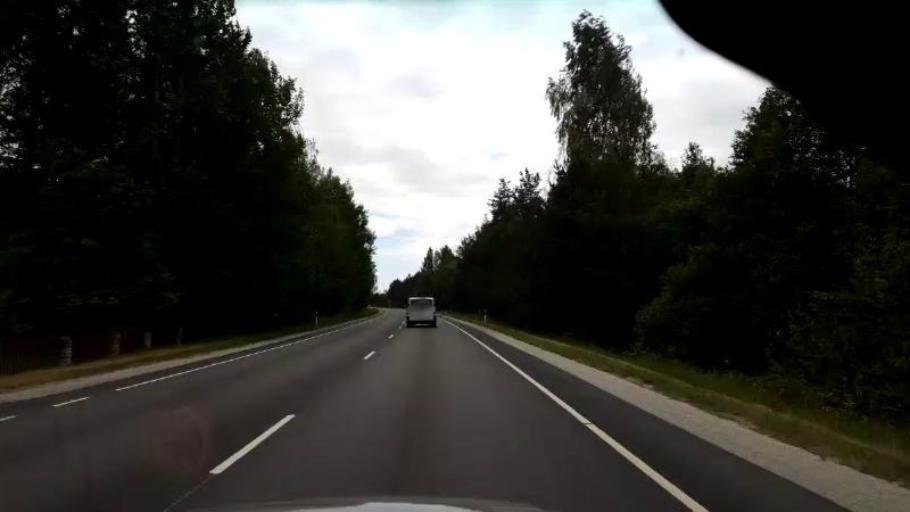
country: EE
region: Paernumaa
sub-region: Paernu linn
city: Parnu
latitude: 58.2127
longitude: 24.4859
